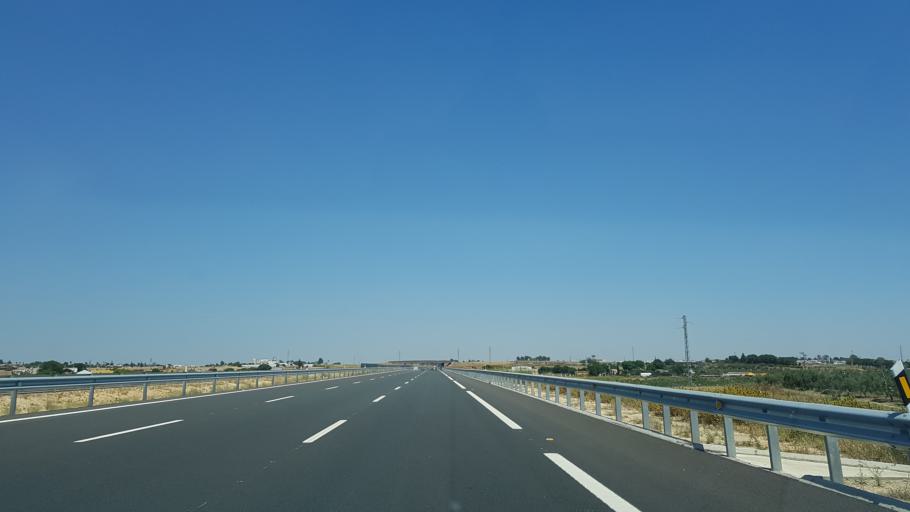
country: ES
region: Andalusia
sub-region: Provincia de Sevilla
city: Coria del Rio
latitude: 37.2954
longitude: -6.0781
